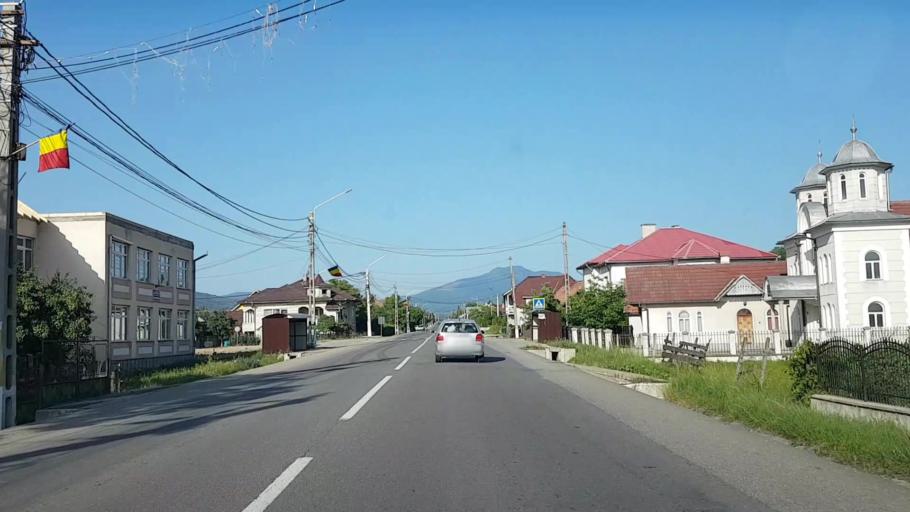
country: RO
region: Bistrita-Nasaud
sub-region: Comuna Josenii Bargaului
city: Mijlocenii Bargaului
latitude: 47.2136
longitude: 24.6880
